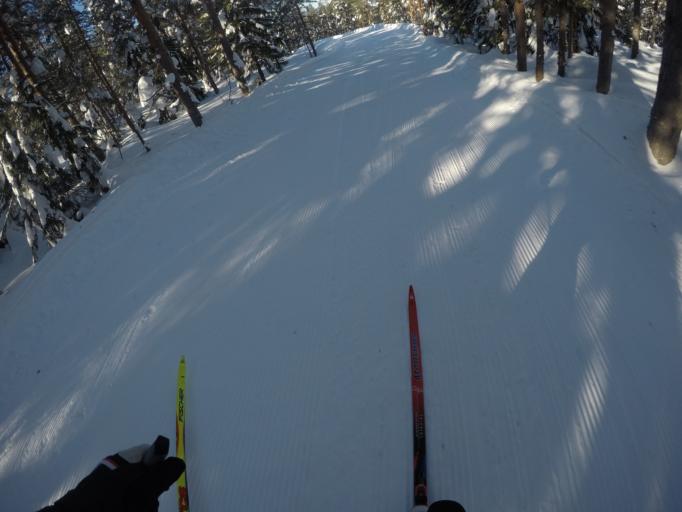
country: SE
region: Vaesternorrland
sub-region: Sundsvalls Kommun
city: Sundsvall
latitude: 62.3667
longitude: 17.3009
